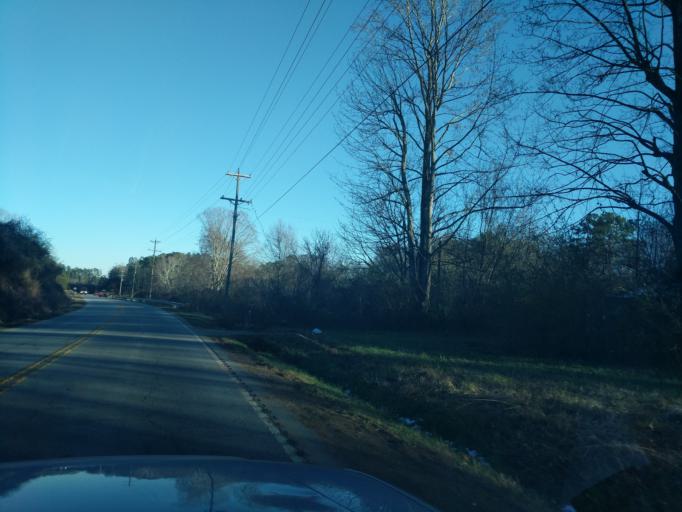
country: US
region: South Carolina
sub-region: Oconee County
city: Westminster
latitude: 34.6884
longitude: -83.1690
